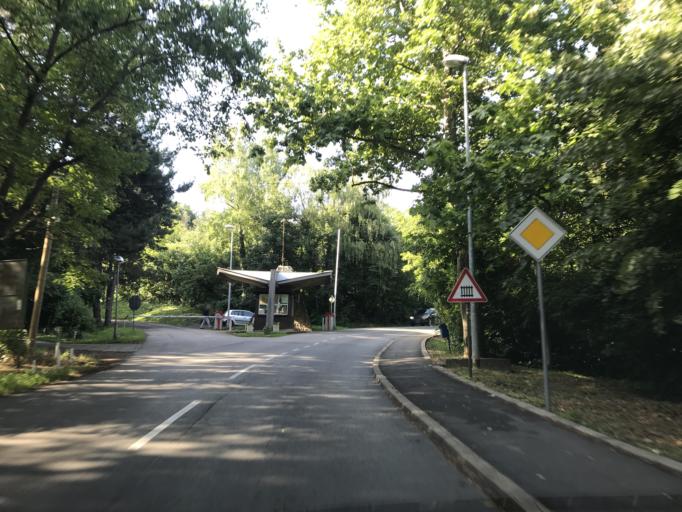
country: RS
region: Autonomna Pokrajina Vojvodina
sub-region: Juznobacki Okrug
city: Petrovaradin
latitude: 45.2220
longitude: 19.8552
